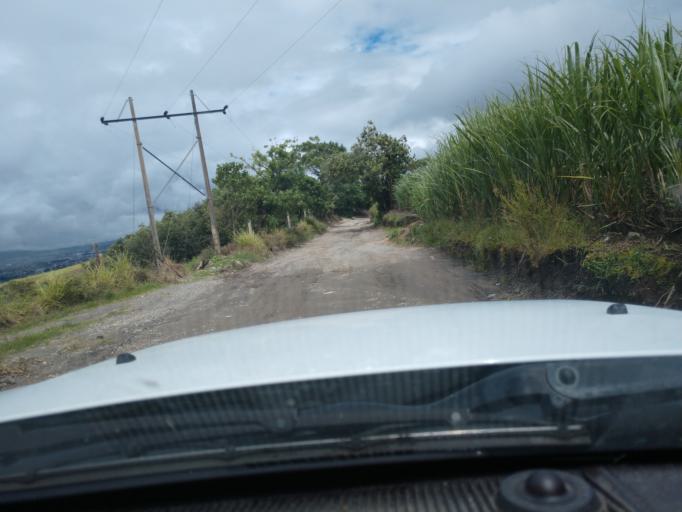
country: MX
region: Nayarit
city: Xalisco
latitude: 21.4386
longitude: -104.9214
